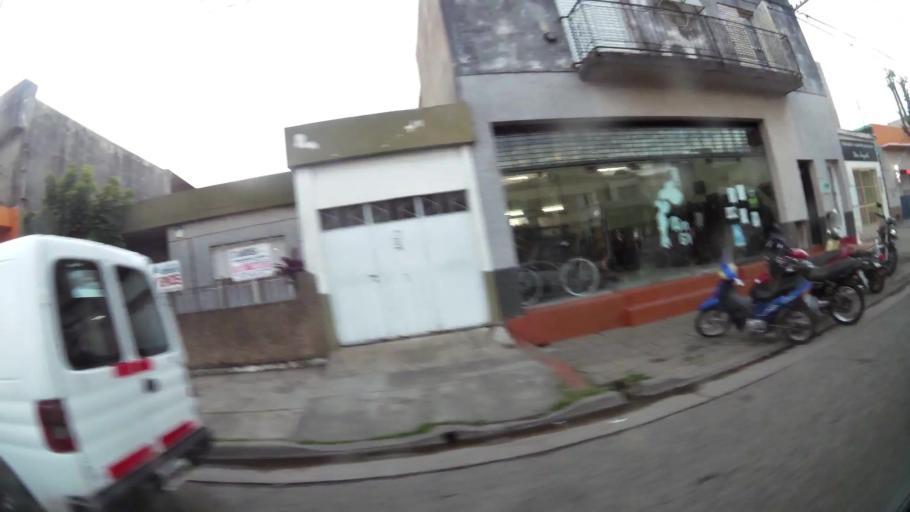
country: AR
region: Buenos Aires
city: San Nicolas de los Arroyos
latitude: -33.3234
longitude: -60.2300
